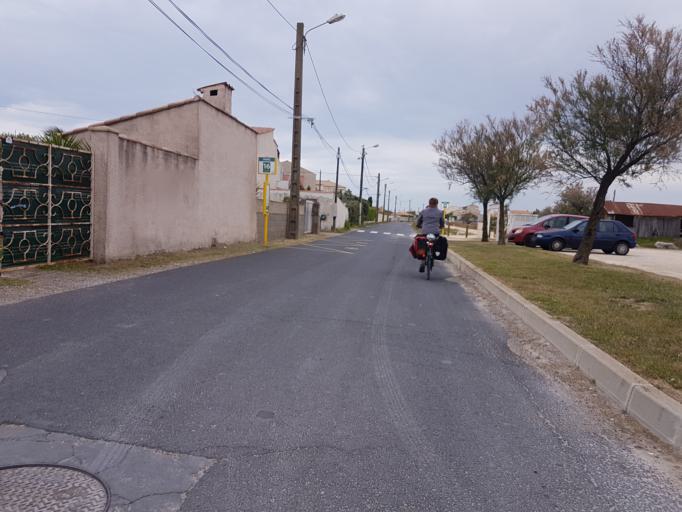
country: FR
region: Languedoc-Roussillon
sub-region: Departement de l'Herault
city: Vic-la-Gardiole
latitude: 43.4488
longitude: 3.8038
